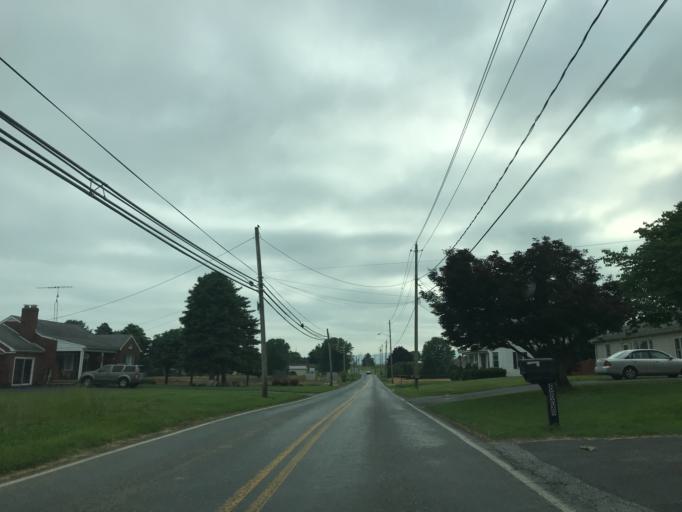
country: US
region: Maryland
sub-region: Frederick County
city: Walkersville
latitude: 39.4843
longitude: -77.3605
